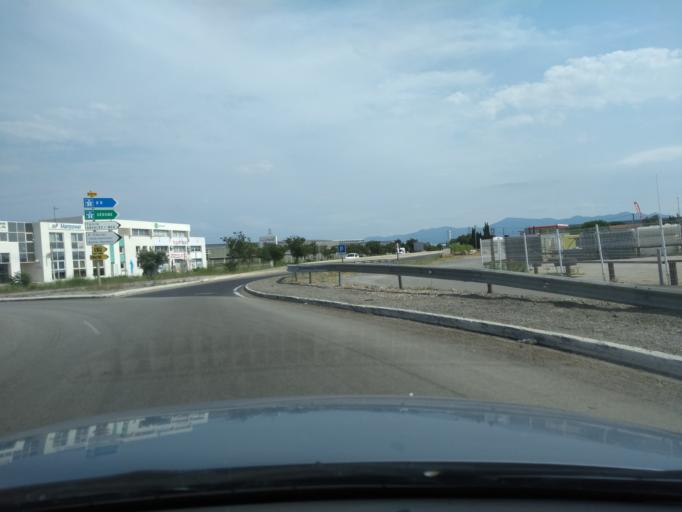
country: FR
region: Languedoc-Roussillon
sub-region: Departement des Pyrenees-Orientales
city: Saint-Esteve
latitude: 42.6908
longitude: 2.8517
